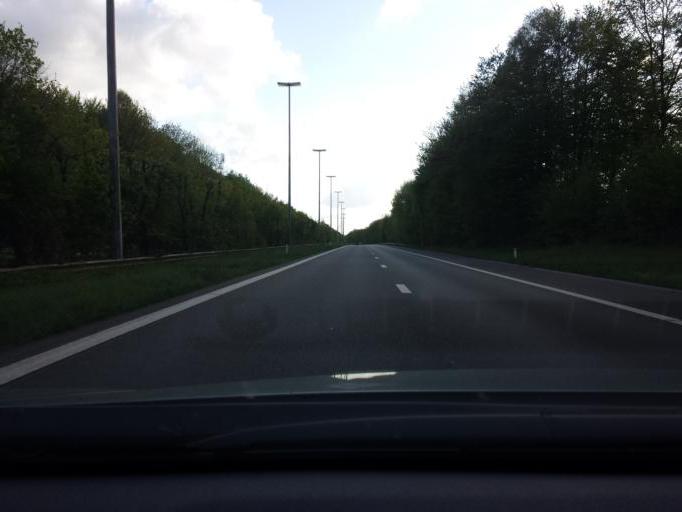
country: BE
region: Wallonia
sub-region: Province de Liege
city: Raeren
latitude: 50.6947
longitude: 6.0694
